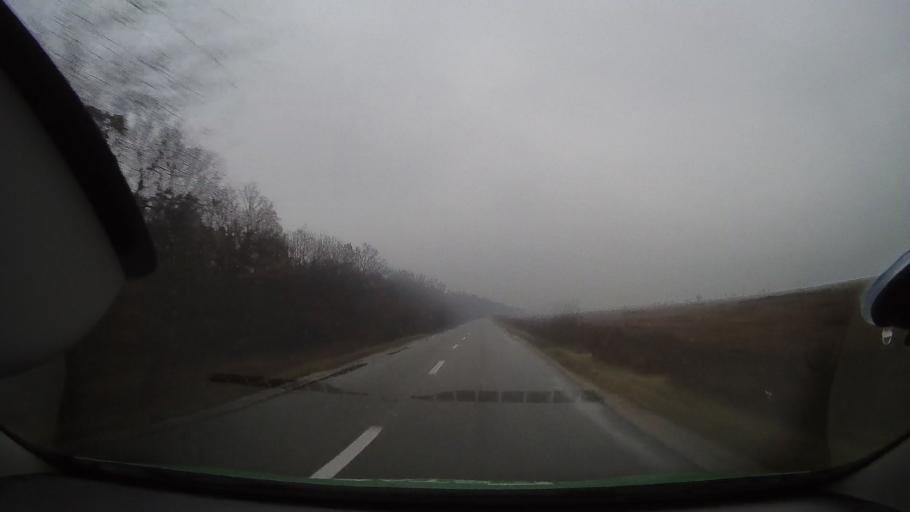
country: RO
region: Bihor
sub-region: Comuna Tinca
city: Gurbediu
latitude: 46.7810
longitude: 21.8709
